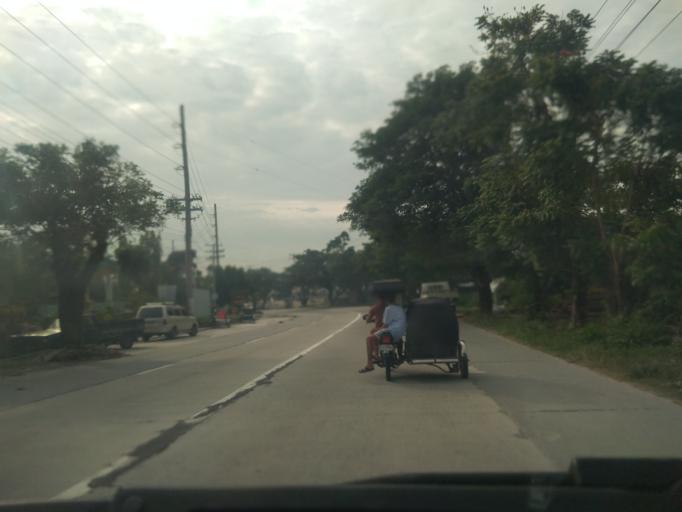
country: PH
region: Central Luzon
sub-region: Province of Pampanga
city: Calibutbut
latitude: 15.1227
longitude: 120.5870
